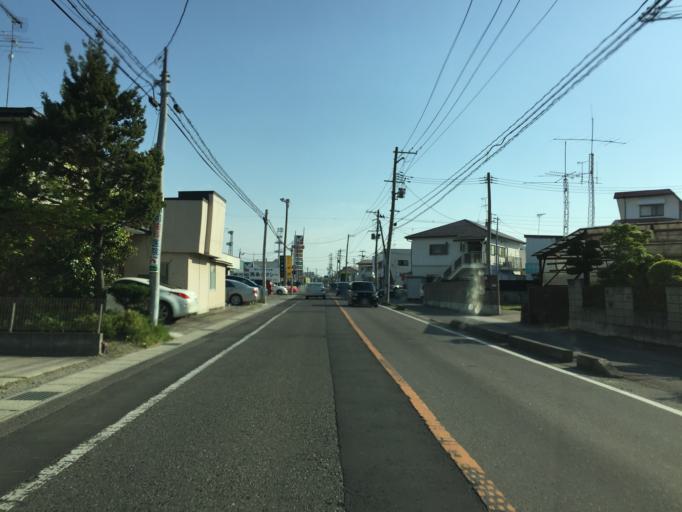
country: JP
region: Fukushima
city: Koriyama
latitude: 37.4036
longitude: 140.3277
